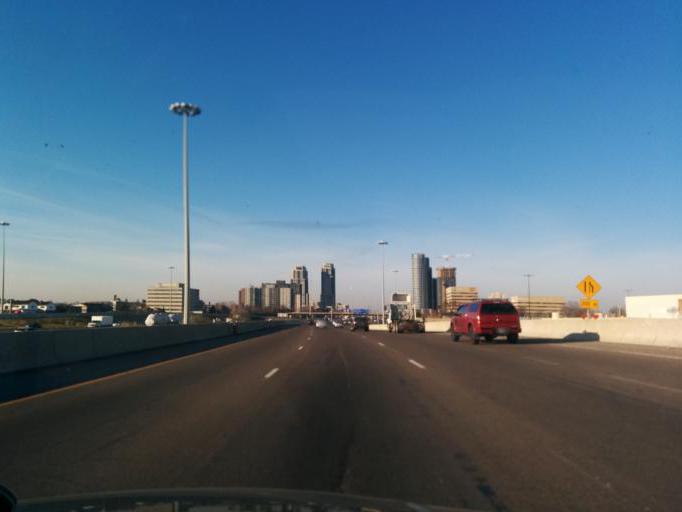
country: CA
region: Ontario
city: Etobicoke
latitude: 43.6311
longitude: -79.5571
